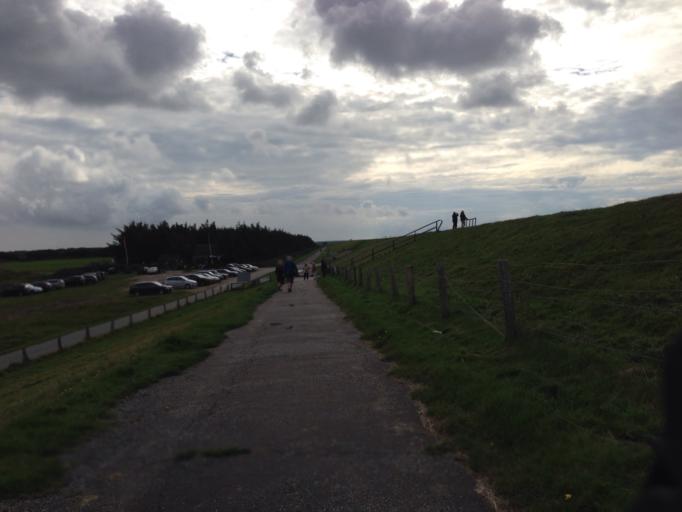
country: DE
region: Schleswig-Holstein
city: Dunsum
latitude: 54.7354
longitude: 8.4107
